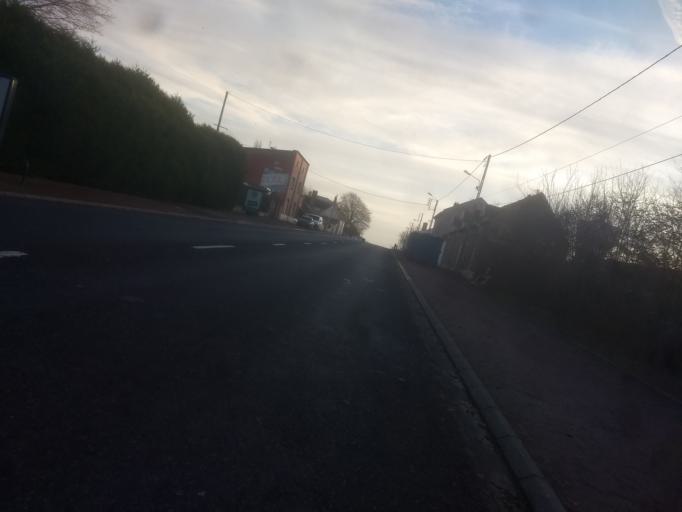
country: FR
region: Nord-Pas-de-Calais
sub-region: Departement du Pas-de-Calais
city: Beaurains
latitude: 50.2596
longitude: 2.7866
